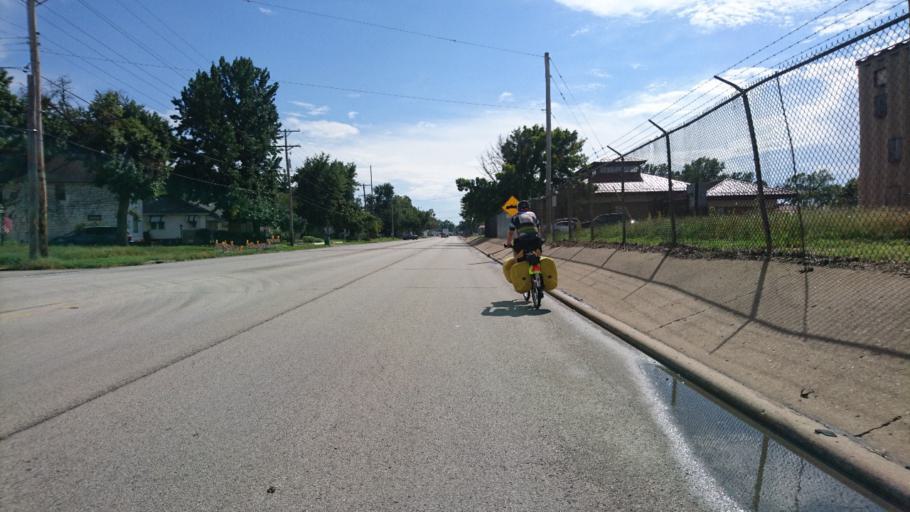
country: US
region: Illinois
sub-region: Sangamon County
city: Grandview
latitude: 39.8359
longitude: -89.6352
